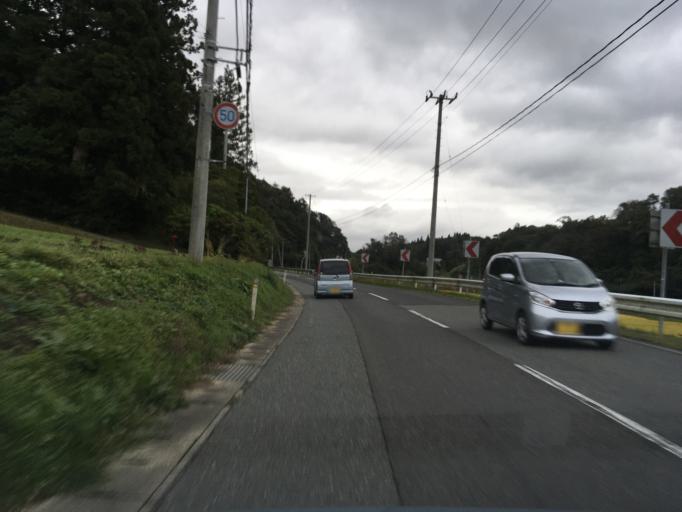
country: JP
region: Iwate
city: Ichinoseki
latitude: 38.9501
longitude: 141.3362
